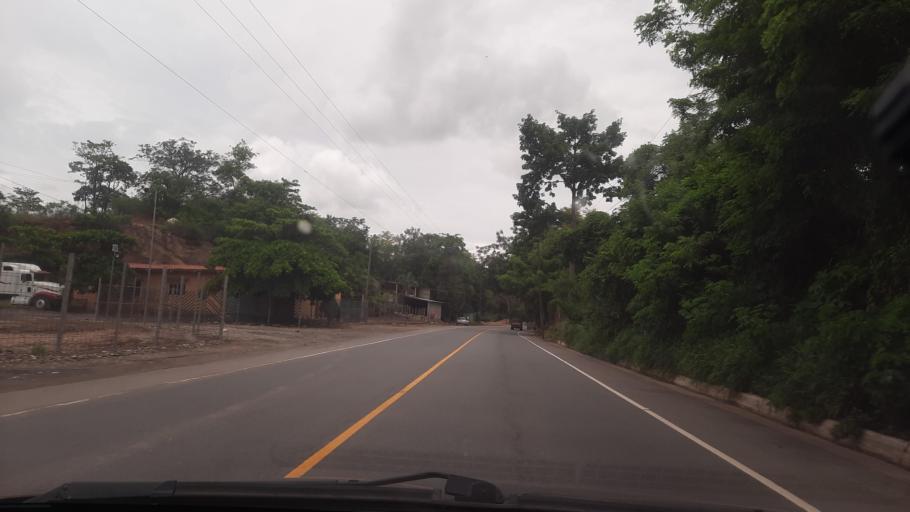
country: GT
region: Zacapa
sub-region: Municipio de Zacapa
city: Gualan
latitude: 15.1659
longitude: -89.3088
